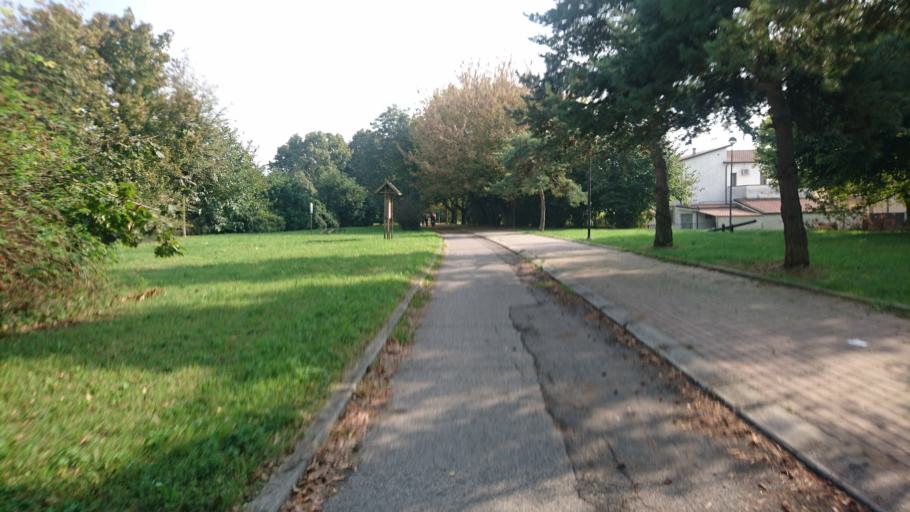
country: IT
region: Veneto
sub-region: Provincia di Rovigo
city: Rovigo
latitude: 45.0675
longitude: 11.7828
